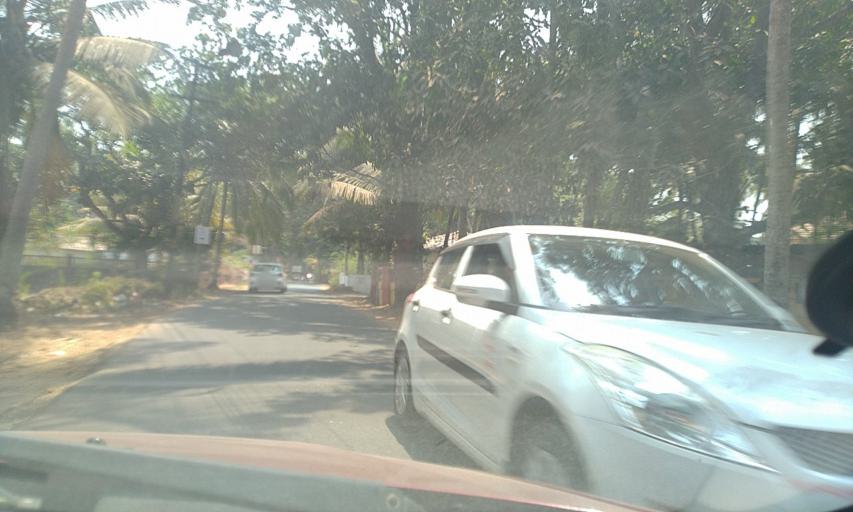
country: IN
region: Goa
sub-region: North Goa
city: Saligao
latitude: 15.5531
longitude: 73.7803
